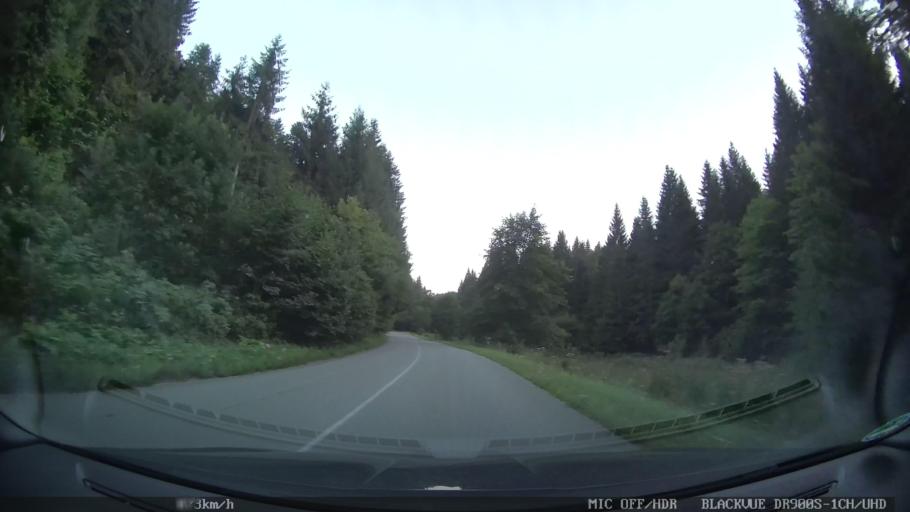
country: HR
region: Primorsko-Goranska
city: Vrbovsko
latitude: 45.2167
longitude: 15.0263
